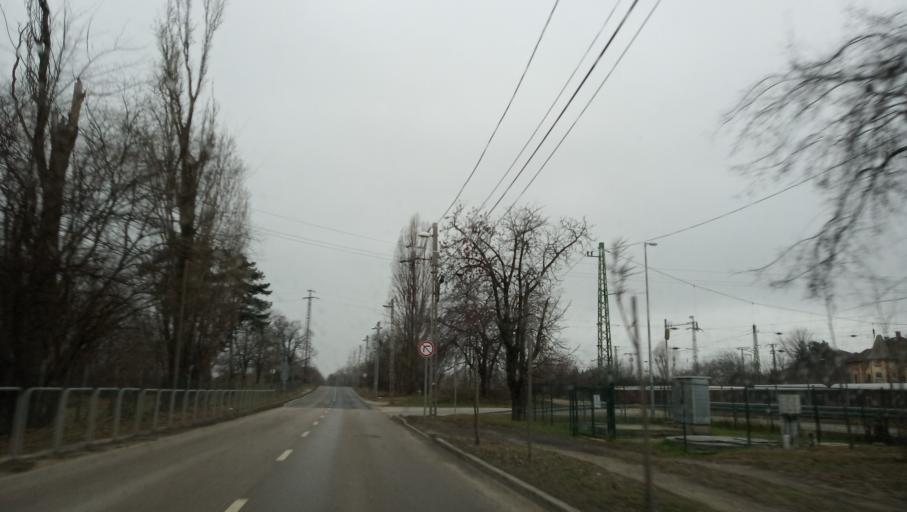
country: HU
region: Pest
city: Dunakeszi
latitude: 47.6244
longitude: 19.1361
